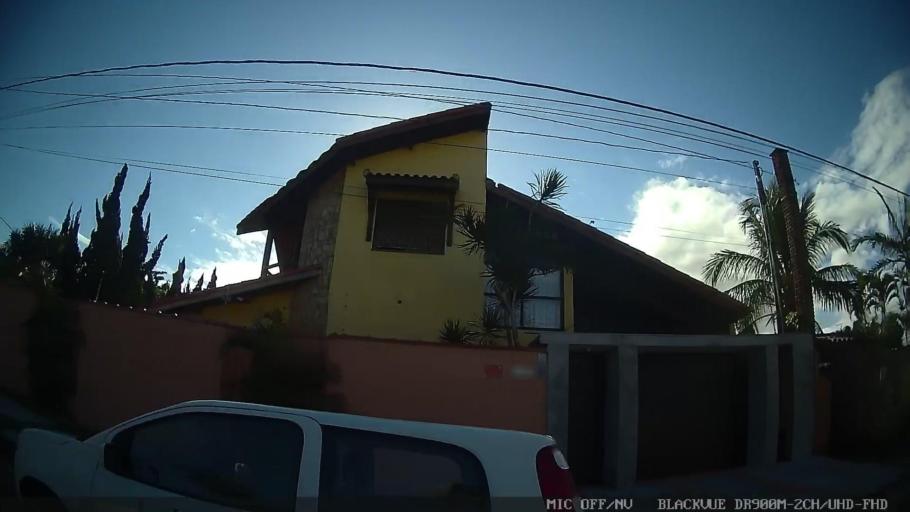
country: BR
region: Sao Paulo
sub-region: Itanhaem
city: Itanhaem
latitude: -24.2169
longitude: -46.8488
